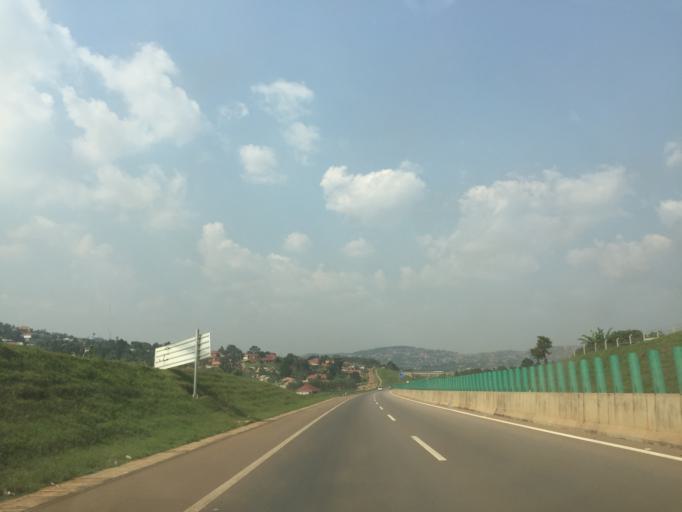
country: UG
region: Central Region
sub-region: Wakiso District
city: Kajansi
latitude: 0.1989
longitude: 32.5263
